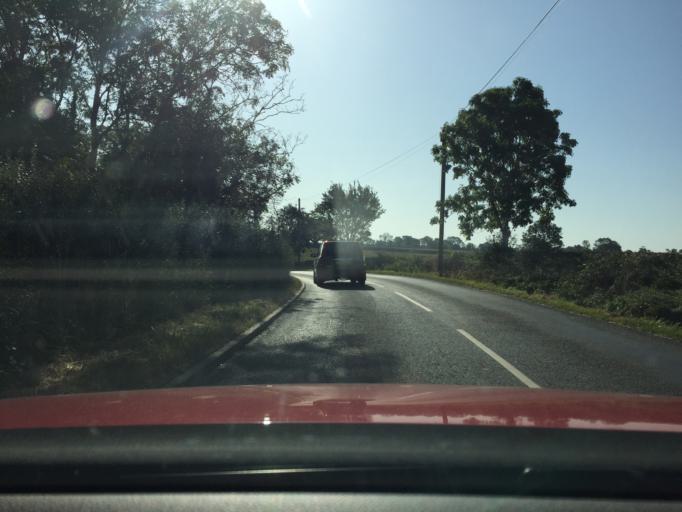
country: GB
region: England
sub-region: Leicestershire
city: Syston
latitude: 52.6688
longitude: -1.0270
